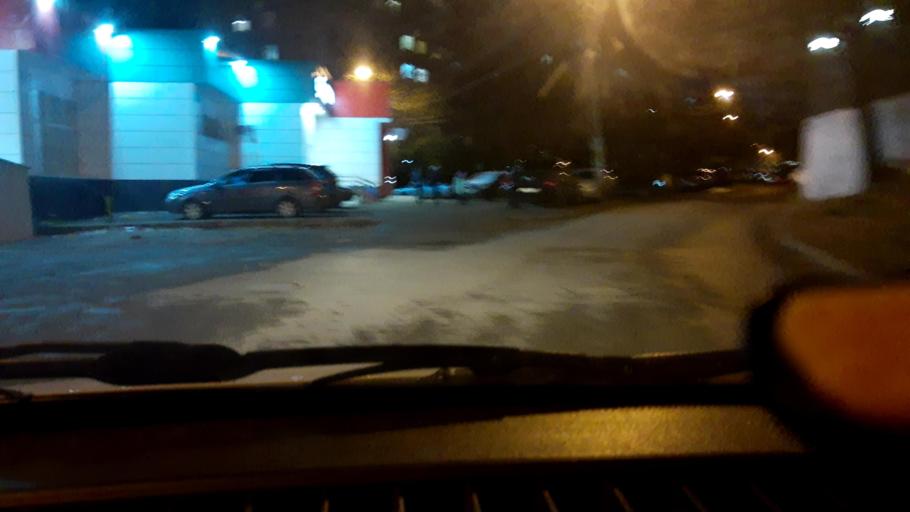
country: RU
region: Bashkortostan
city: Ufa
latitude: 54.7369
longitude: 55.9949
